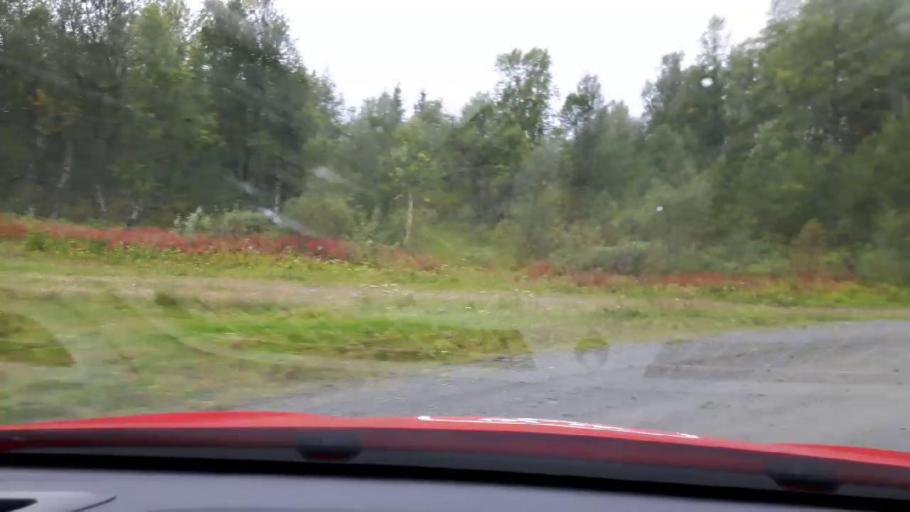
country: NO
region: Nord-Trondelag
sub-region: Meraker
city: Meraker
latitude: 63.5701
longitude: 12.2829
